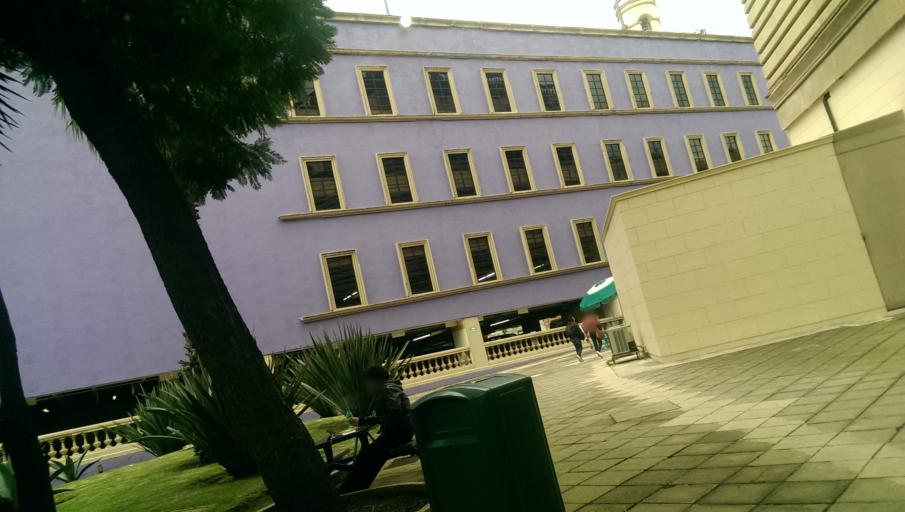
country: MX
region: Mexico City
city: Tlalpan
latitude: 19.2833
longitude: -99.1369
